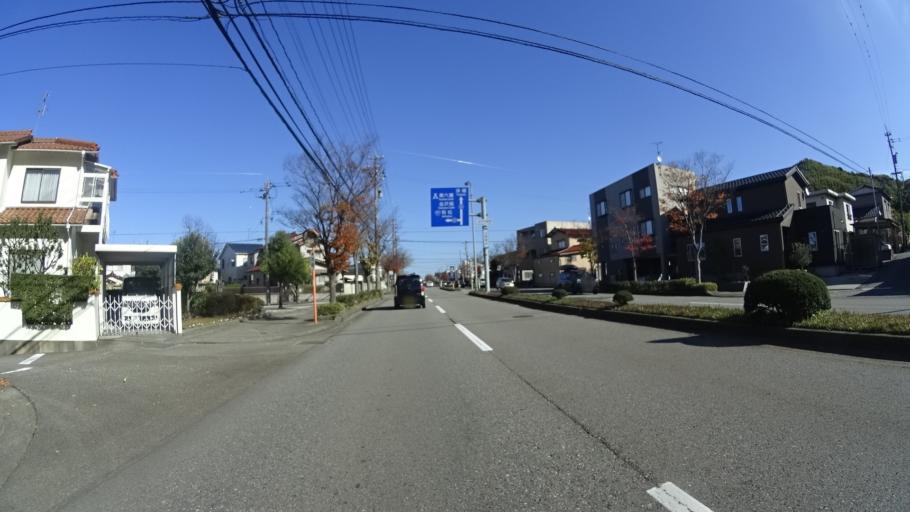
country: JP
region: Ishikawa
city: Nonoichi
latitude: 36.5221
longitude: 136.6399
